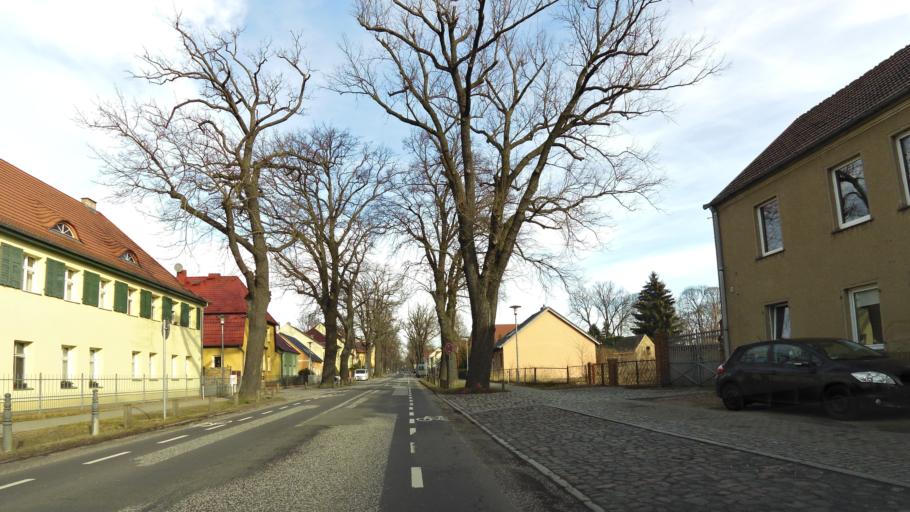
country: DE
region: Brandenburg
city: Michendorf
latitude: 52.3134
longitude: 13.0307
